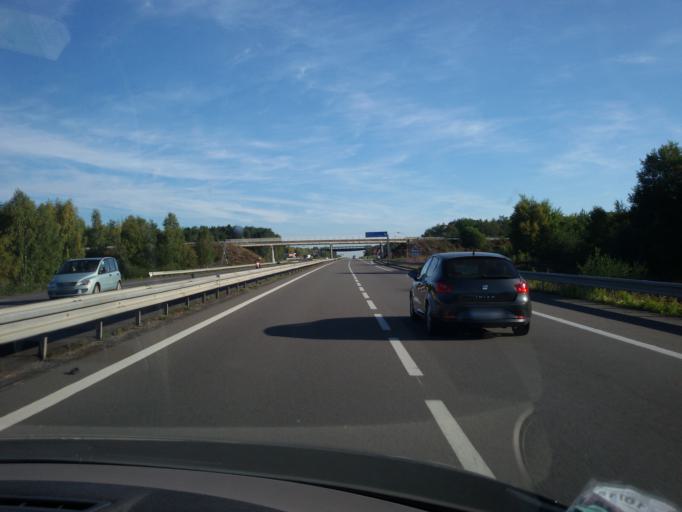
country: FR
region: Centre
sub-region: Departement du Loir-et-Cher
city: Theillay
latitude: 47.3433
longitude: 2.0482
